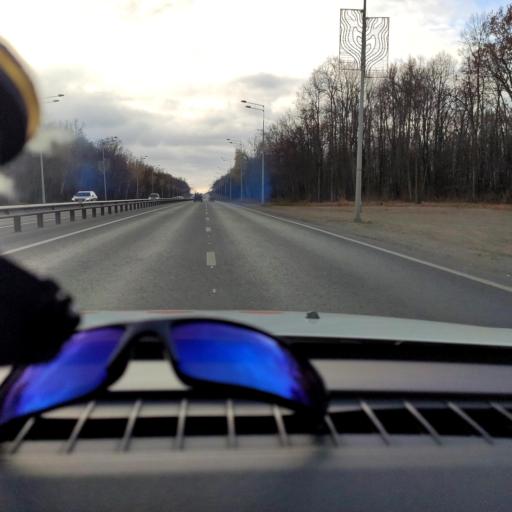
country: RU
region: Samara
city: Novosemeykino
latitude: 53.3284
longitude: 50.2312
